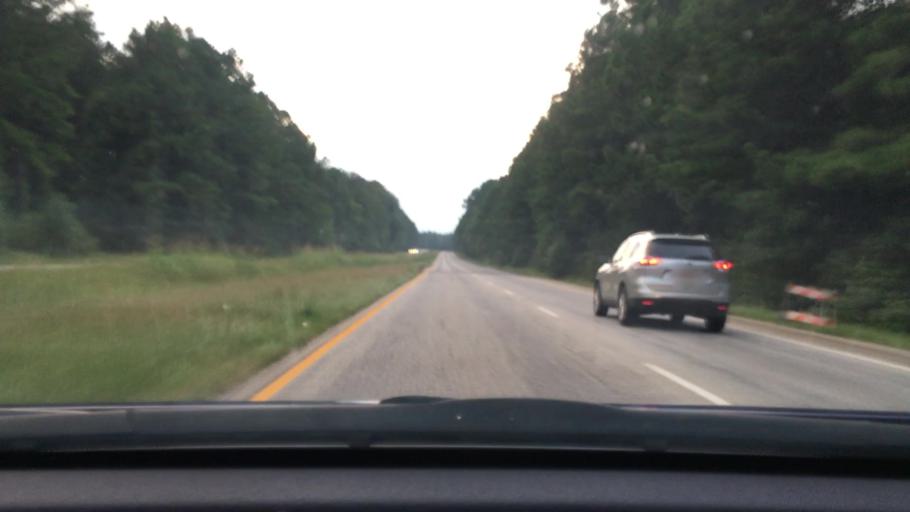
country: US
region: South Carolina
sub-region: Sumter County
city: Stateburg
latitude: 33.9502
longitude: -80.5530
